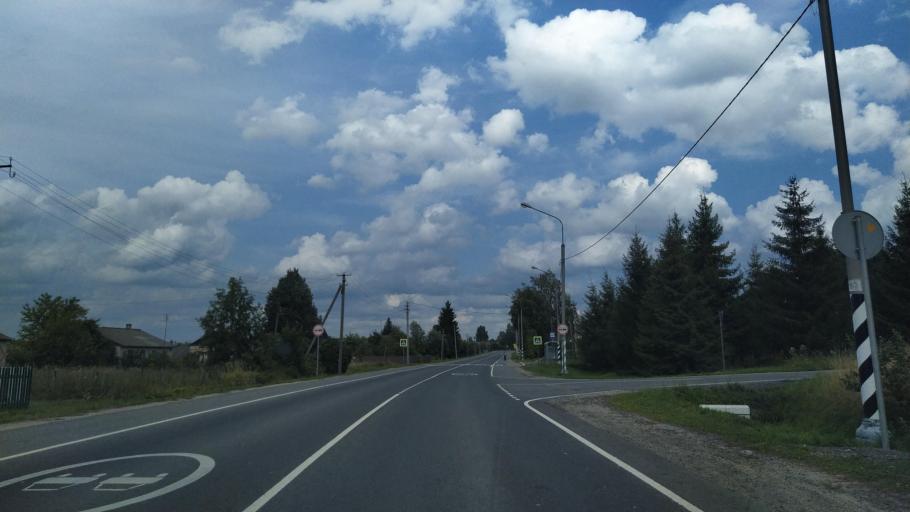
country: RU
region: Pskov
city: Dno
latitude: 58.0600
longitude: 29.9790
